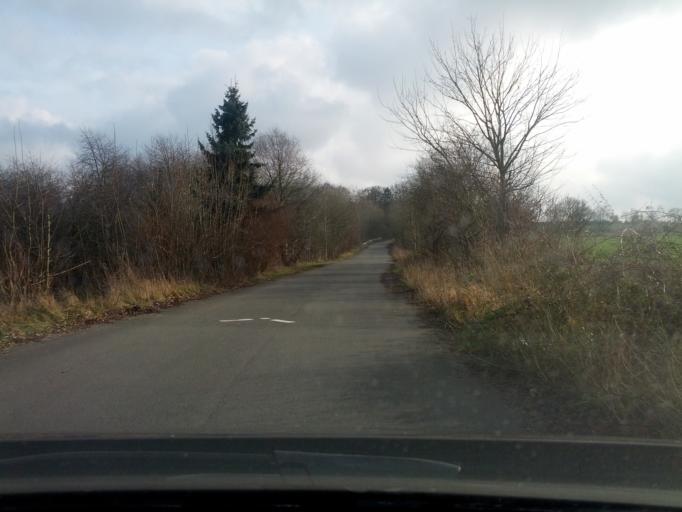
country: DE
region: Lower Saxony
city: Furstenberg
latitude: 51.7393
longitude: 9.4025
